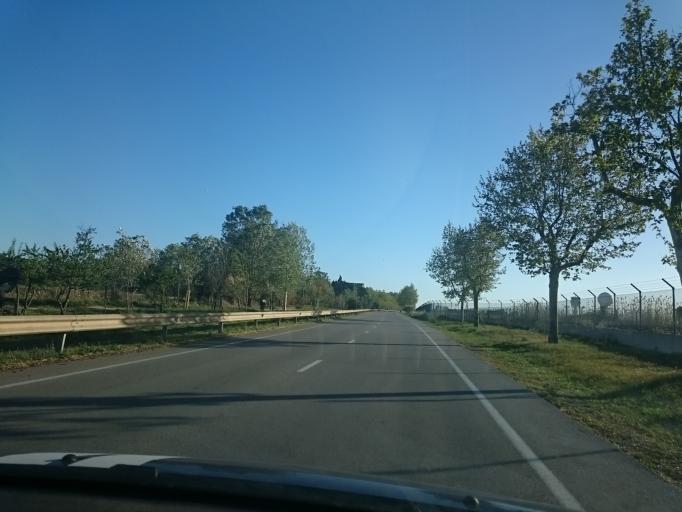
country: ES
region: Catalonia
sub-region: Provincia de Barcelona
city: El Prat de Llobregat
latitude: 41.3035
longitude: 2.1064
